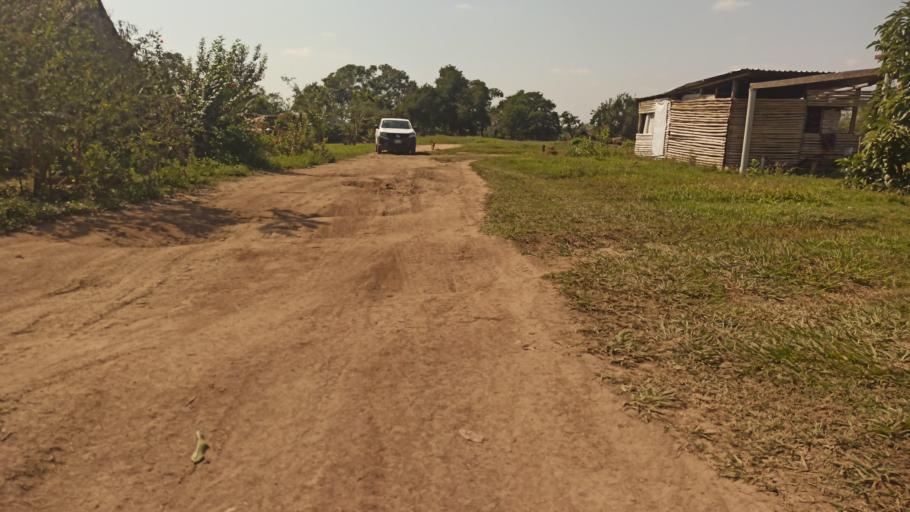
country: MX
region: Puebla
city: San Jose Acateno
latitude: 20.1629
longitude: -97.1654
